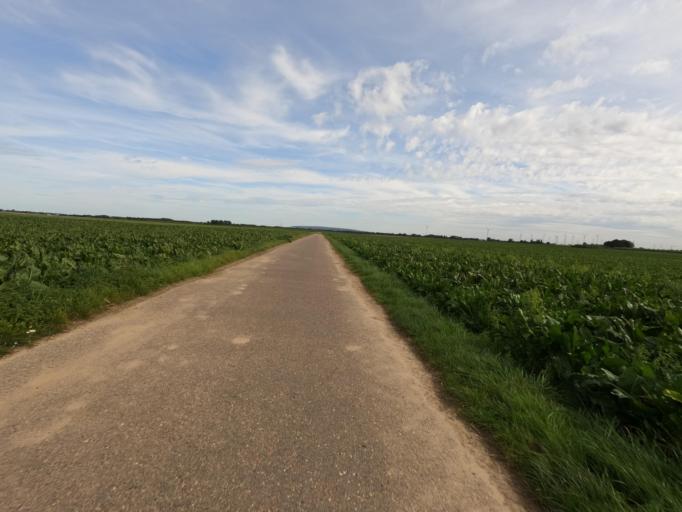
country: DE
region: North Rhine-Westphalia
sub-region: Regierungsbezirk Koln
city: Linnich
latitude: 50.9607
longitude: 6.2309
